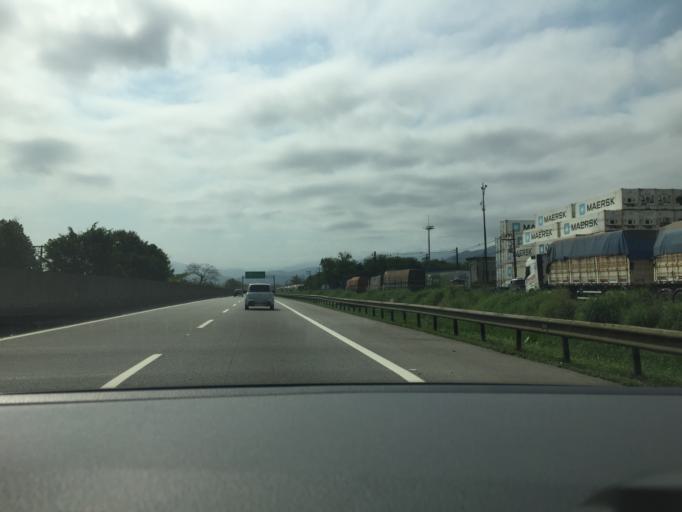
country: BR
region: Sao Paulo
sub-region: Guaruja
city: Guaruja
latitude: -23.9500
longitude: -46.2772
